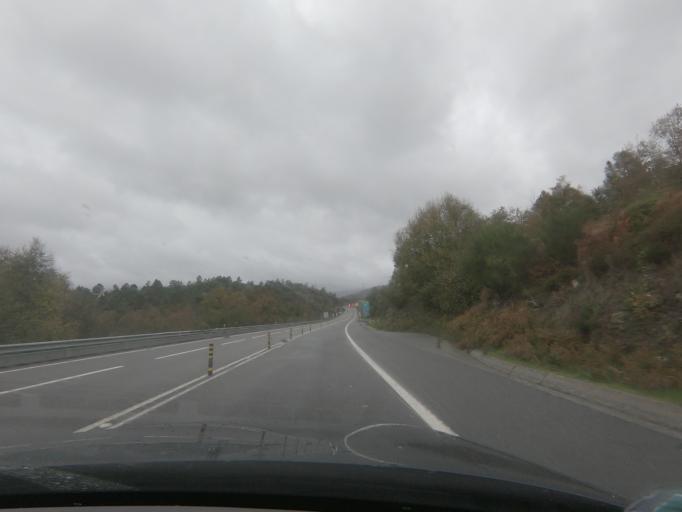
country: PT
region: Vila Real
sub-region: Santa Marta de Penaguiao
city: Santa Marta de Penaguiao
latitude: 41.2838
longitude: -7.8246
